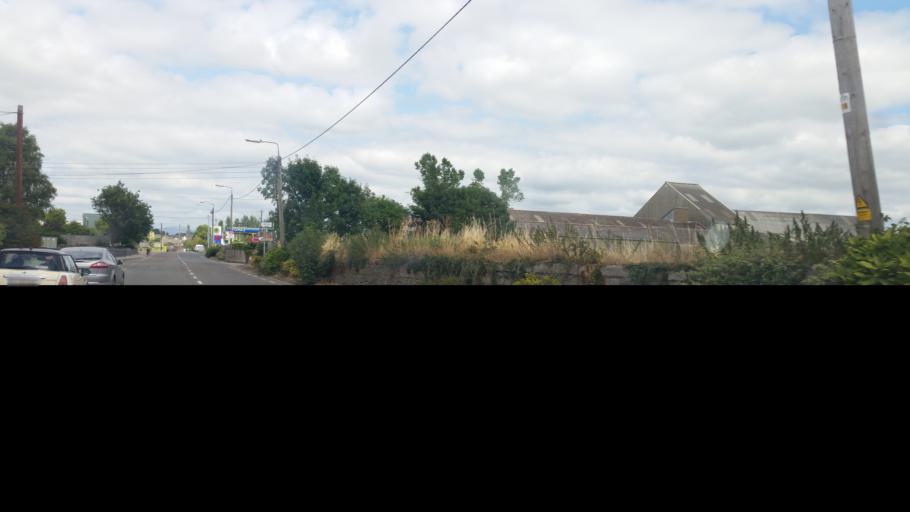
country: IE
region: Leinster
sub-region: County Carlow
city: Tullow
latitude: 52.7972
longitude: -6.7454
